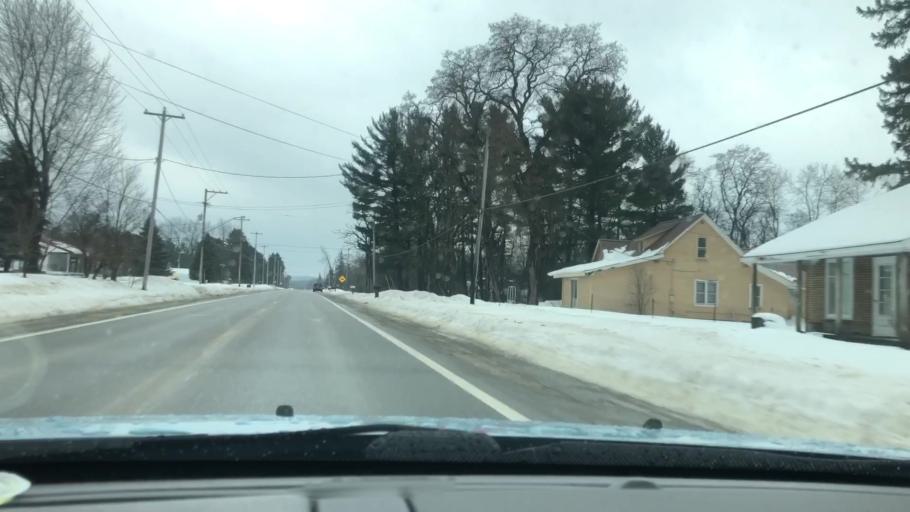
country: US
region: Michigan
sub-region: Charlevoix County
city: East Jordan
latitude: 45.1461
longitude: -85.1192
